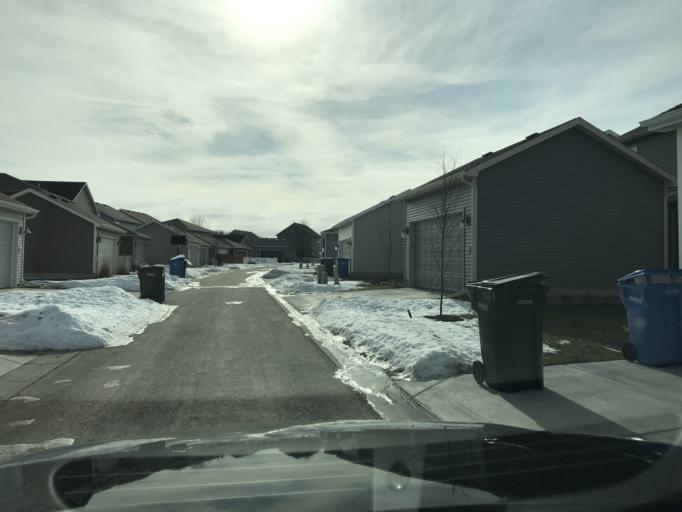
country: US
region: Wisconsin
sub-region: Dane County
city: Monona
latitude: 43.0929
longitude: -89.2739
